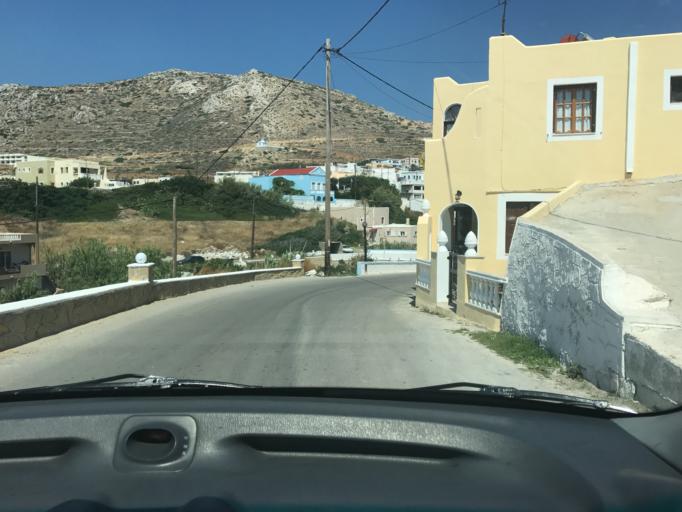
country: GR
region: South Aegean
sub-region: Nomos Dodekanisou
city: Karpathos
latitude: 35.4774
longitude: 27.1178
